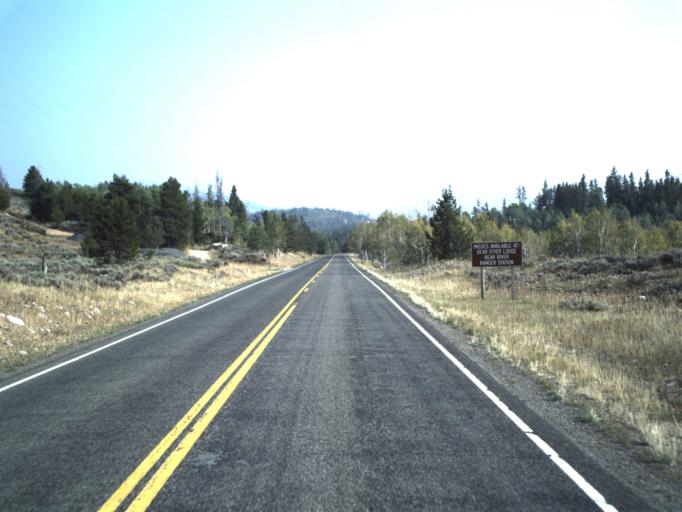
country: US
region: Wyoming
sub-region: Uinta County
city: Evanston
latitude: 40.9320
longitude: -110.8323
